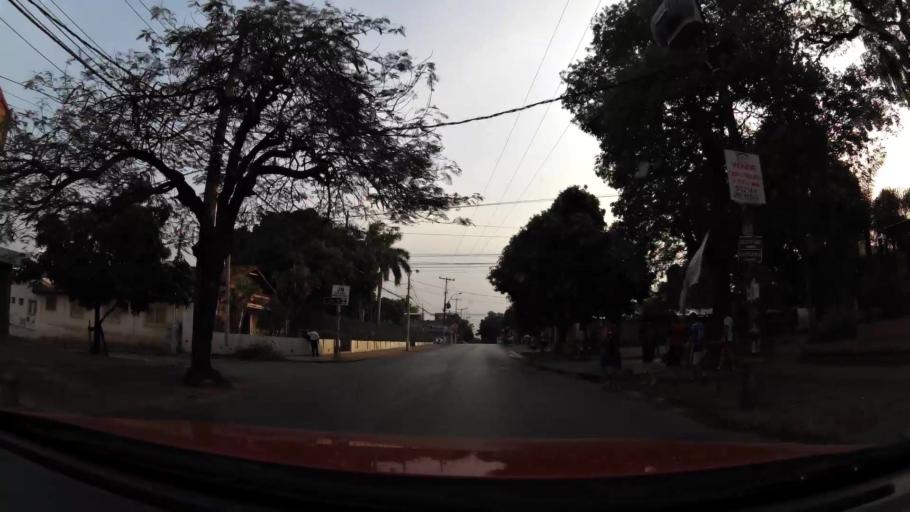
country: PY
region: Central
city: Lambare
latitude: -25.3235
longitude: -57.5803
